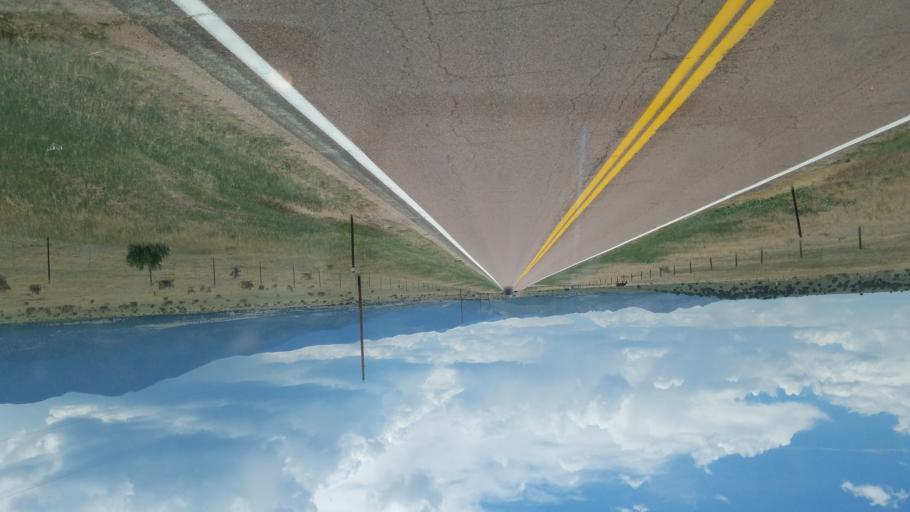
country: US
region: Colorado
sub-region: Fremont County
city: Florence
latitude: 38.2889
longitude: -105.0875
